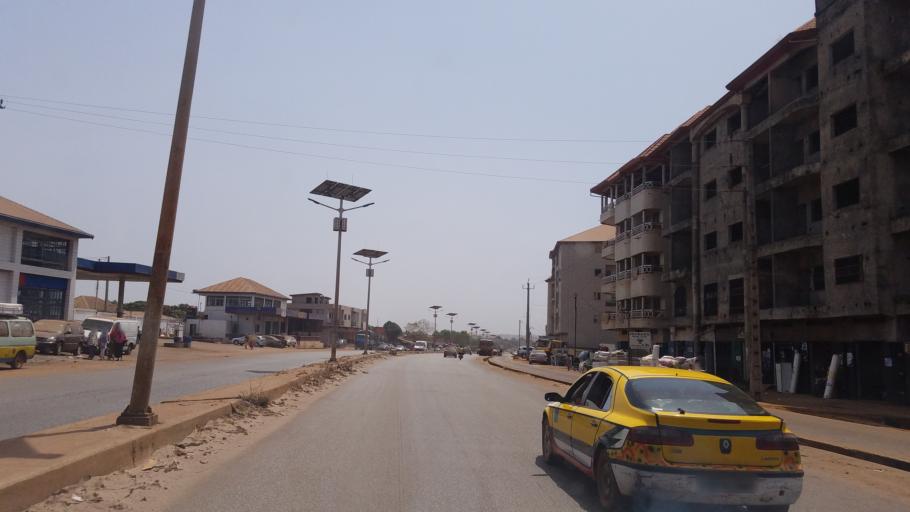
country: GN
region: Kindia
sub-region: Prefecture de Dubreka
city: Dubreka
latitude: 9.6631
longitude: -13.5637
